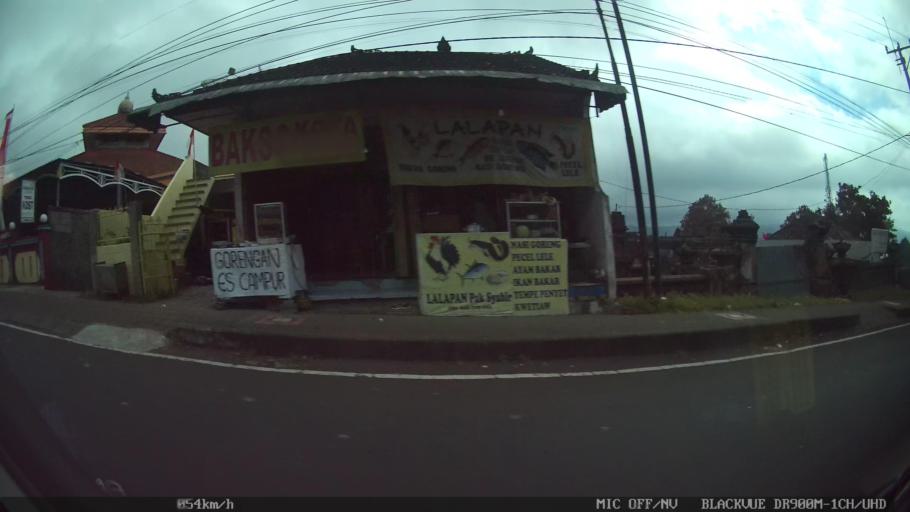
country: ID
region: Bali
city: Bantiran
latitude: -8.3140
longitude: 115.0047
